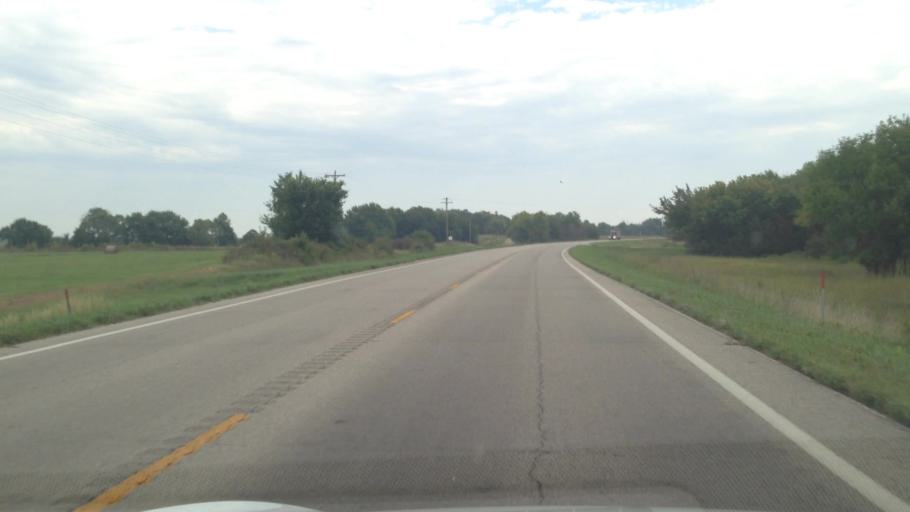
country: US
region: Kansas
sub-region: Bourbon County
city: Fort Scott
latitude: 37.8923
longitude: -95.0451
